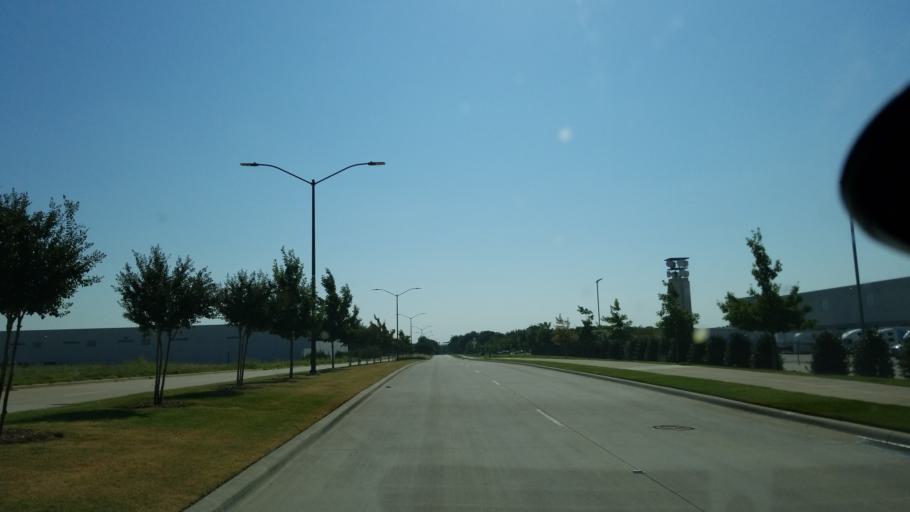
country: US
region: Texas
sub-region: Tarrant County
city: Euless
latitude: 32.8340
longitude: -97.0533
